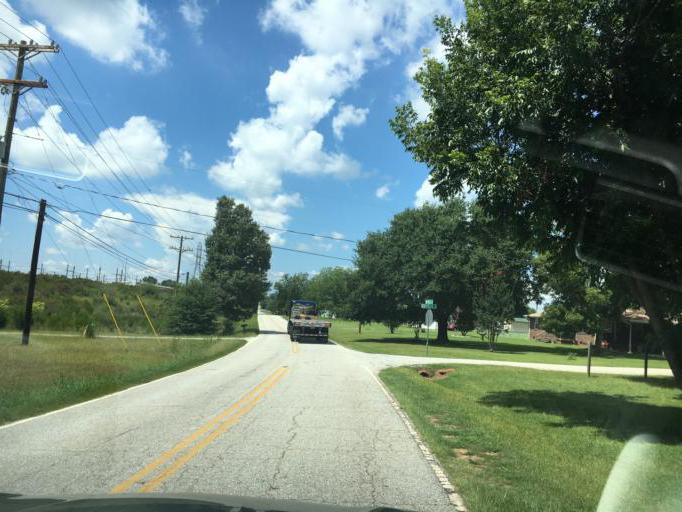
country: US
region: South Carolina
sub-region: Spartanburg County
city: Duncan
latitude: 34.9025
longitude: -82.1439
